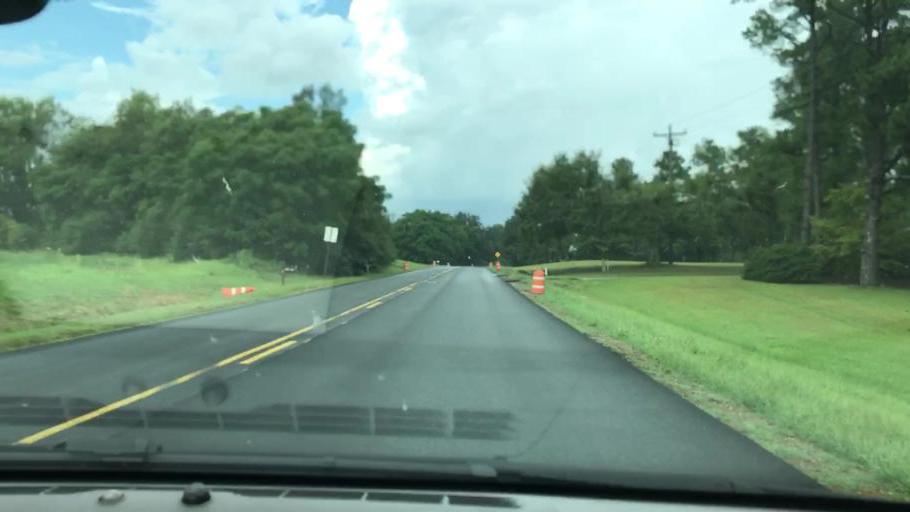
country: US
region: Georgia
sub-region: Early County
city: Blakely
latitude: 31.4046
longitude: -84.9608
